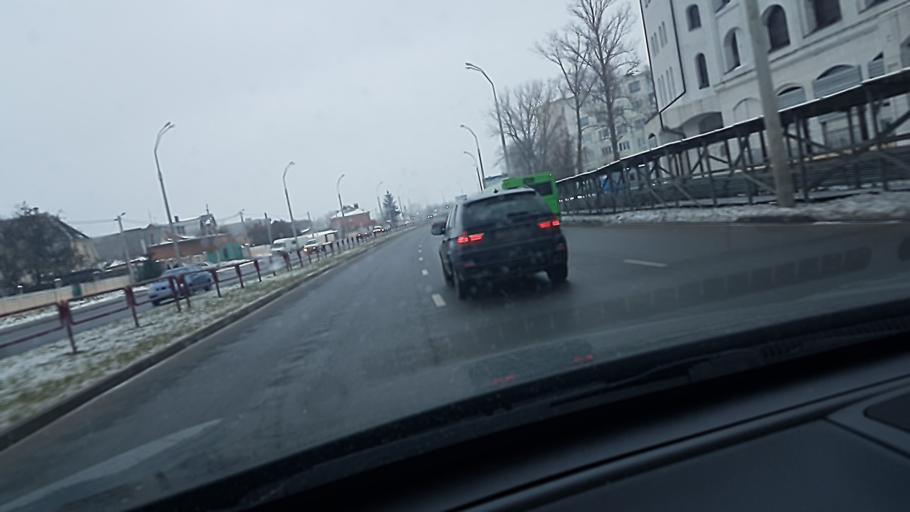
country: BY
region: Minsk
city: Bal'shavik
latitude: 53.9559
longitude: 27.5353
